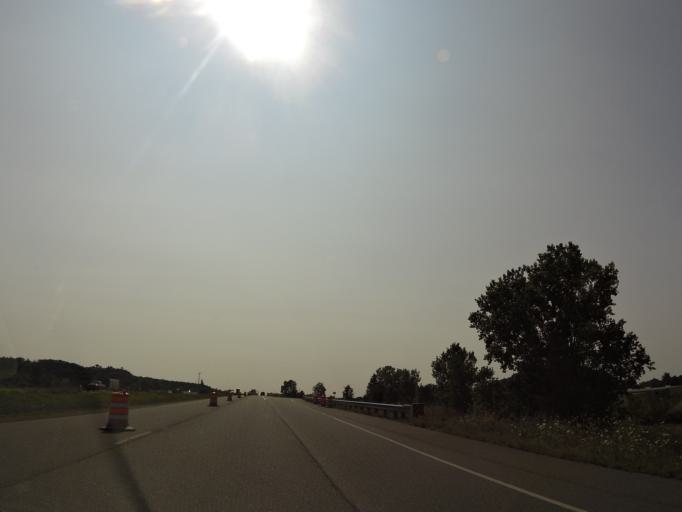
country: US
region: Wisconsin
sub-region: Monroe County
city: Tomah
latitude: 43.9743
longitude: -90.4696
